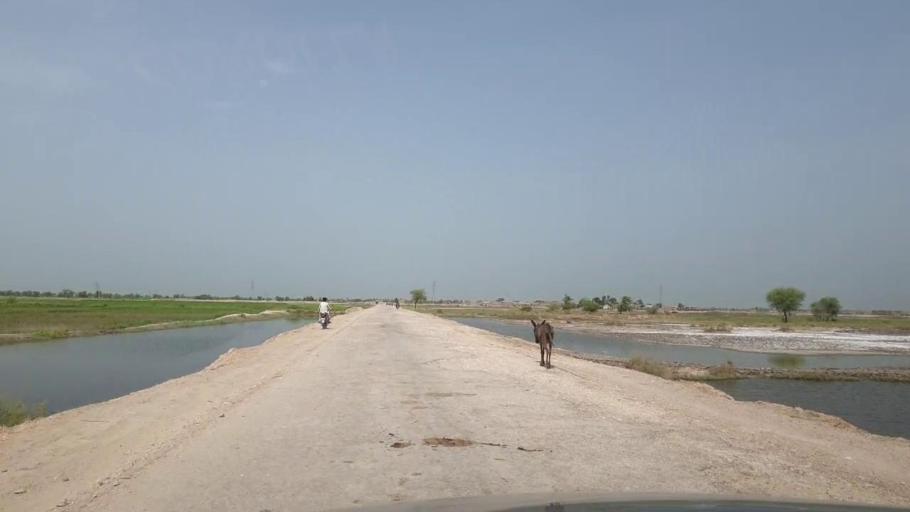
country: PK
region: Sindh
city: Garhi Yasin
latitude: 27.8540
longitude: 68.4336
